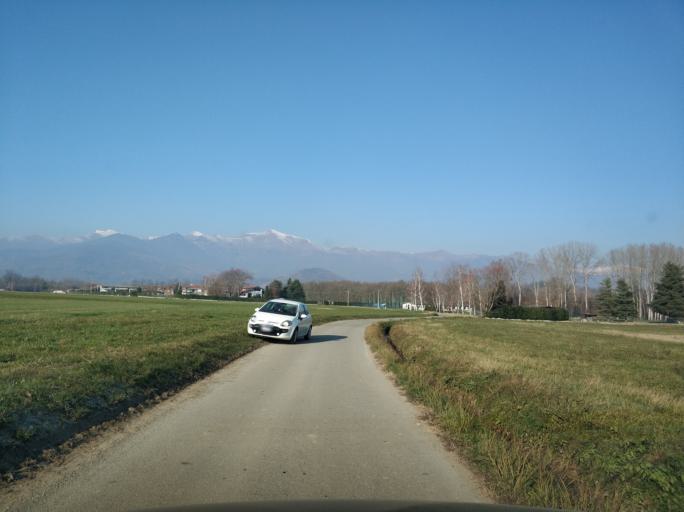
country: IT
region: Piedmont
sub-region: Provincia di Torino
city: Barbania
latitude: 45.3074
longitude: 7.6439
